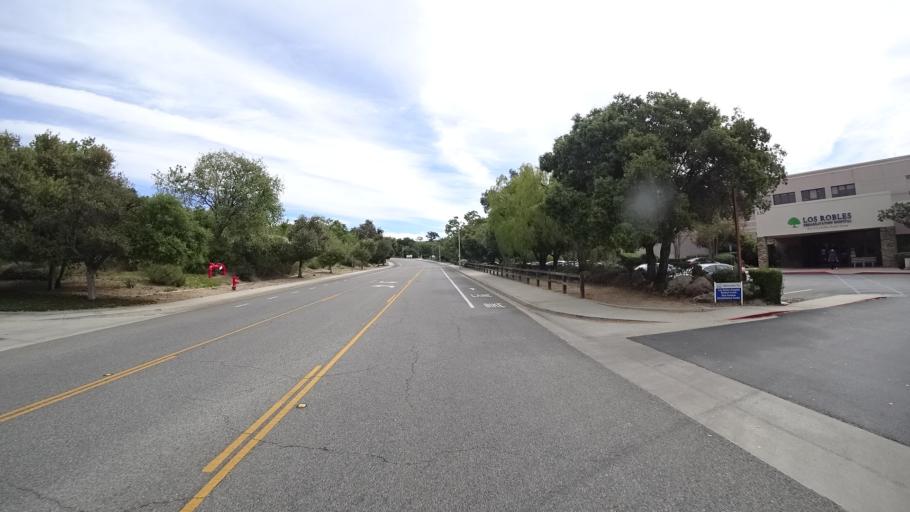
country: US
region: California
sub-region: Los Angeles County
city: Westlake Village
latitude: 34.1555
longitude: -118.8163
